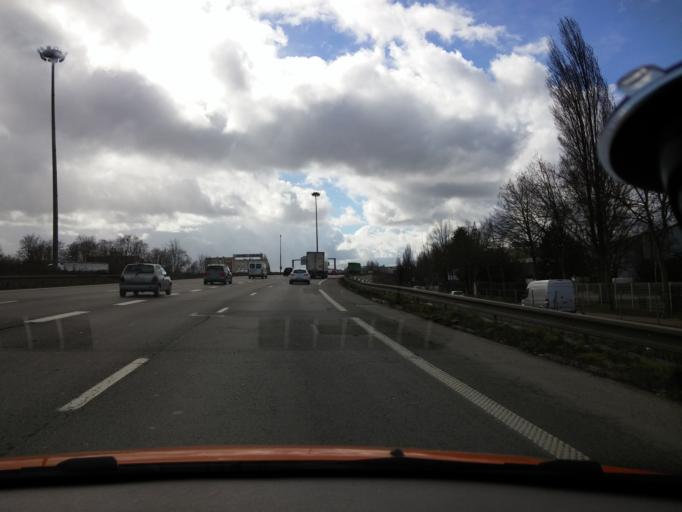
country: FR
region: Ile-de-France
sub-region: Departement de l'Essonne
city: Wissous
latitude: 48.7359
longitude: 2.3154
